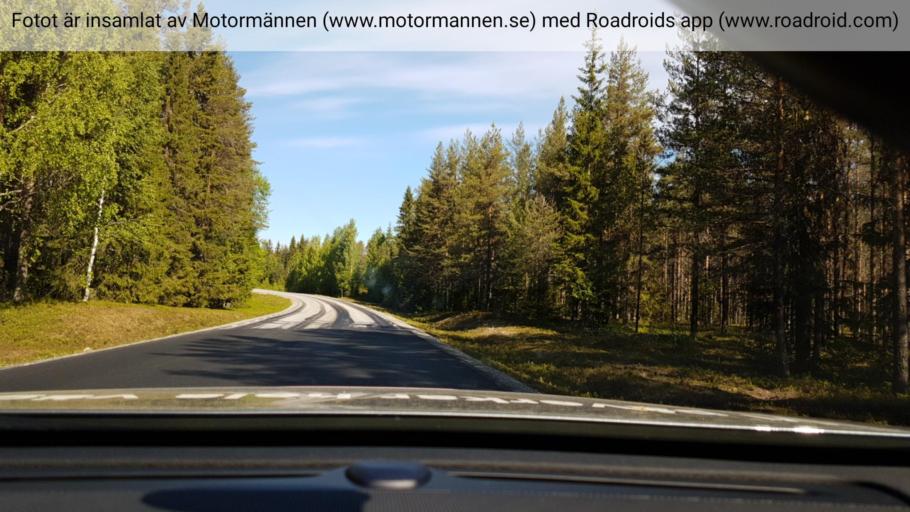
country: SE
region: Vaesterbotten
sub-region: Bjurholms Kommun
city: Bjurholm
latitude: 63.9980
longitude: 18.7897
